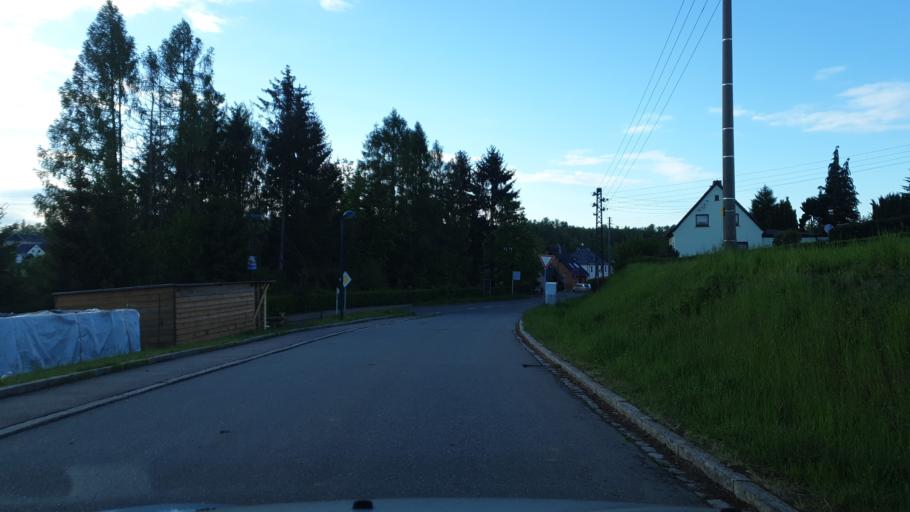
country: DE
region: Saxony
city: Oelsnitz
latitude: 50.7336
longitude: 12.7134
